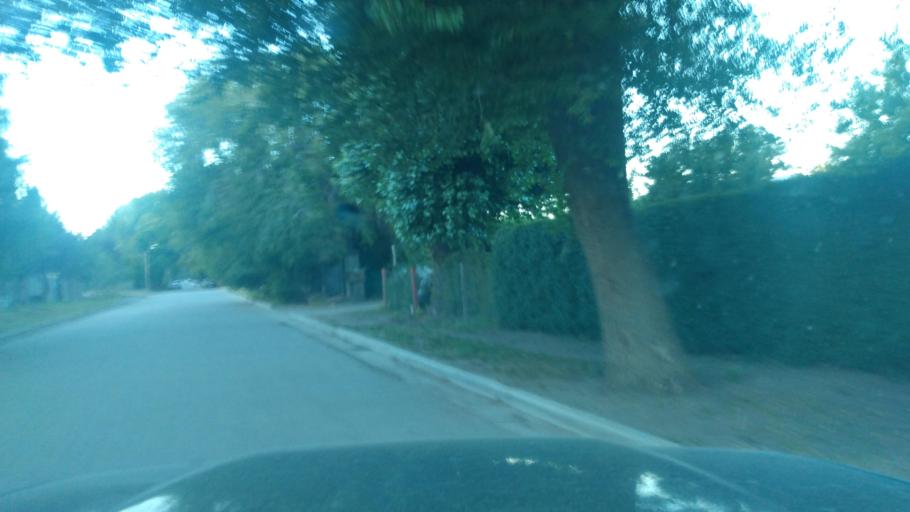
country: AR
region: Neuquen
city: Junin de los Andes
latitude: -39.9550
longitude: -71.0746
